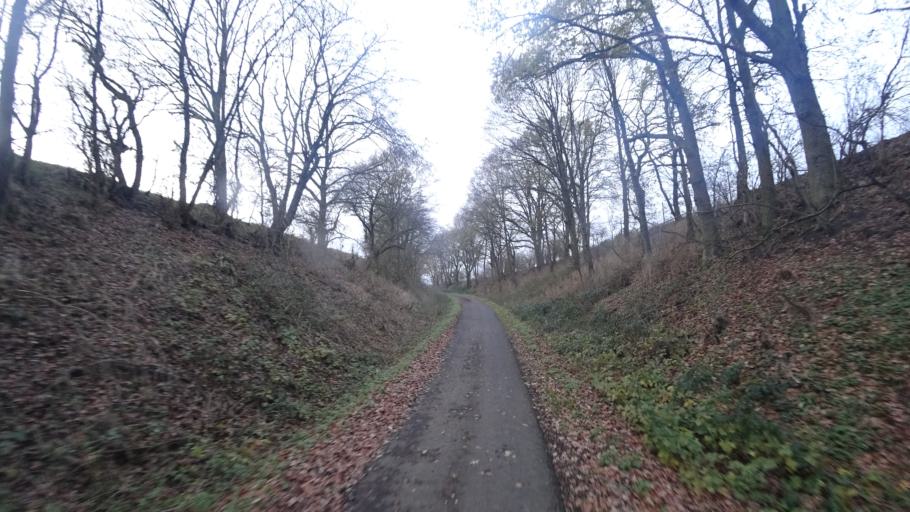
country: DE
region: Rheinland-Pfalz
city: Bassenheim
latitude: 50.3557
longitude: 7.4421
